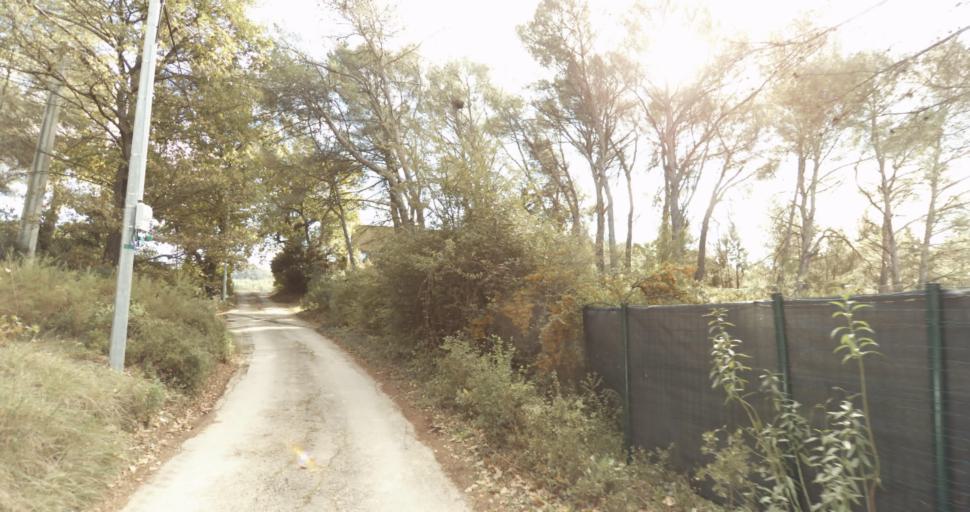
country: FR
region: Provence-Alpes-Cote d'Azur
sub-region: Departement des Bouches-du-Rhone
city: Venelles
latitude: 43.6117
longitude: 5.4922
